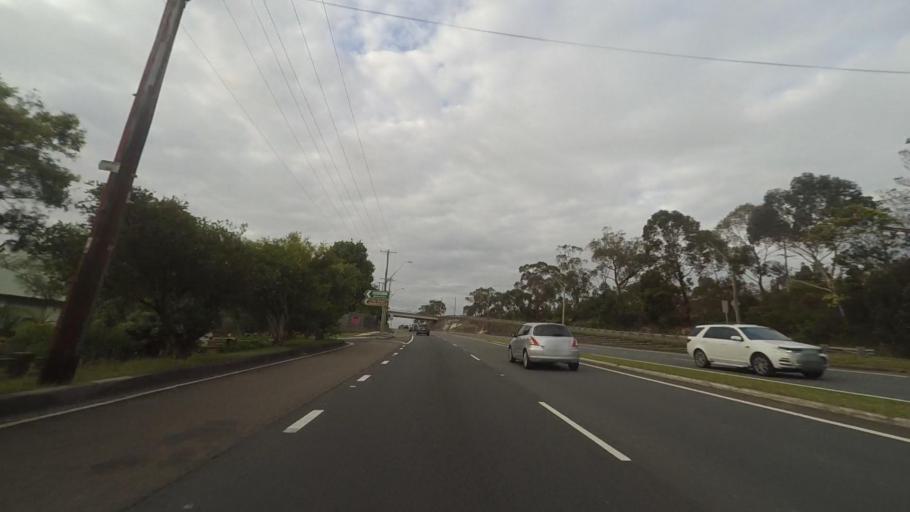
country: AU
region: New South Wales
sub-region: Wollongong
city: Helensburgh
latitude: -34.1372
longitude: 150.9943
